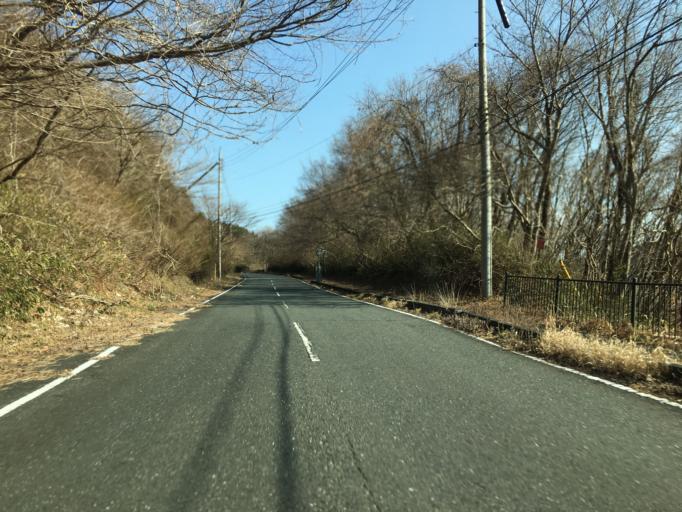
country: JP
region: Ibaraki
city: Kitaibaraki
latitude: 36.8047
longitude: 140.6362
